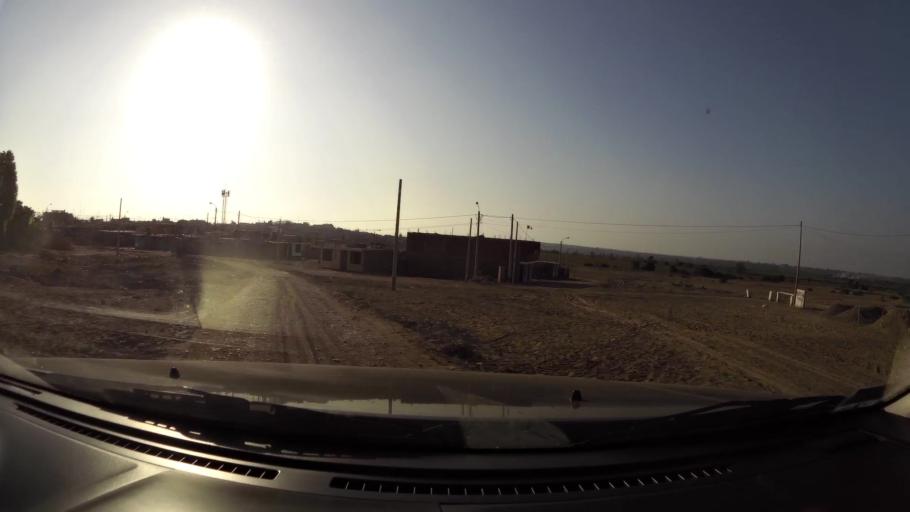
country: PE
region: Ica
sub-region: Provincia de Pisco
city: Villa Tupac Amaru
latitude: -13.7094
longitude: -76.1430
